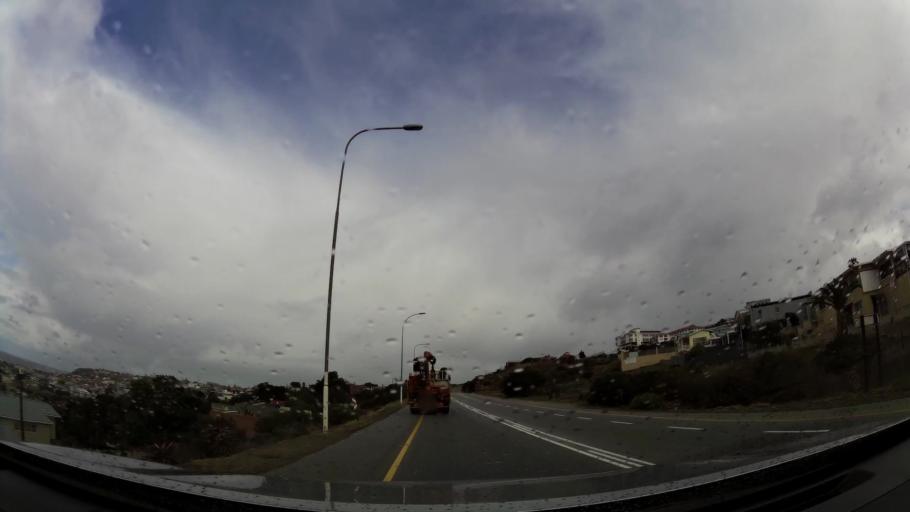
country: ZA
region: Western Cape
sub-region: Eden District Municipality
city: Mossel Bay
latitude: -34.1780
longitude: 22.1323
